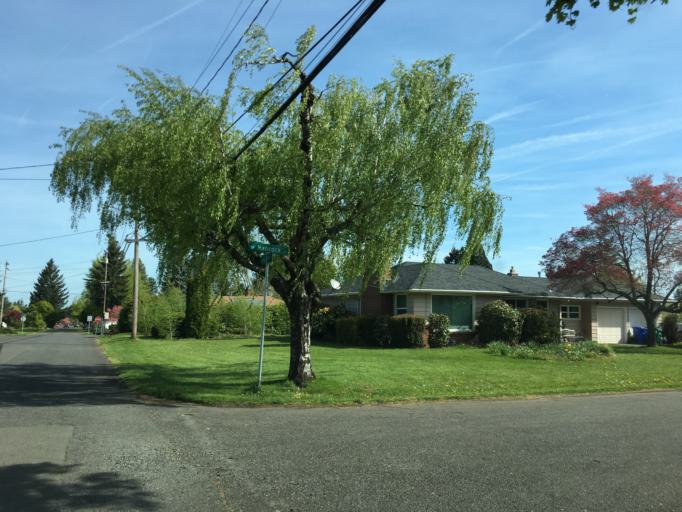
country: US
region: Oregon
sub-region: Multnomah County
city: Lents
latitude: 45.5363
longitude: -122.5244
